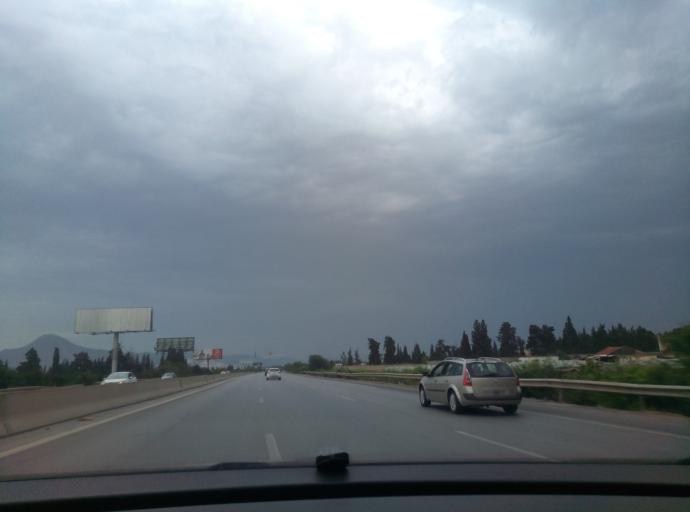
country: TN
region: Tunis
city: Rades
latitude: 36.7230
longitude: 10.2595
